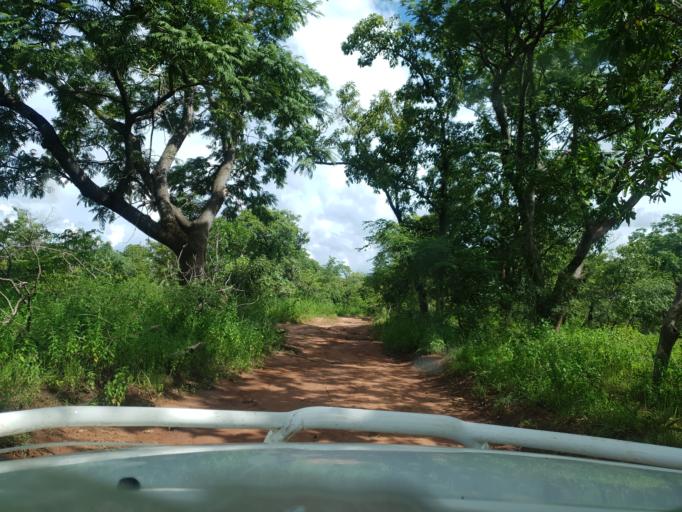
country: CI
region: Savanes
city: Tengrela
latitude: 10.4625
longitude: -6.7969
